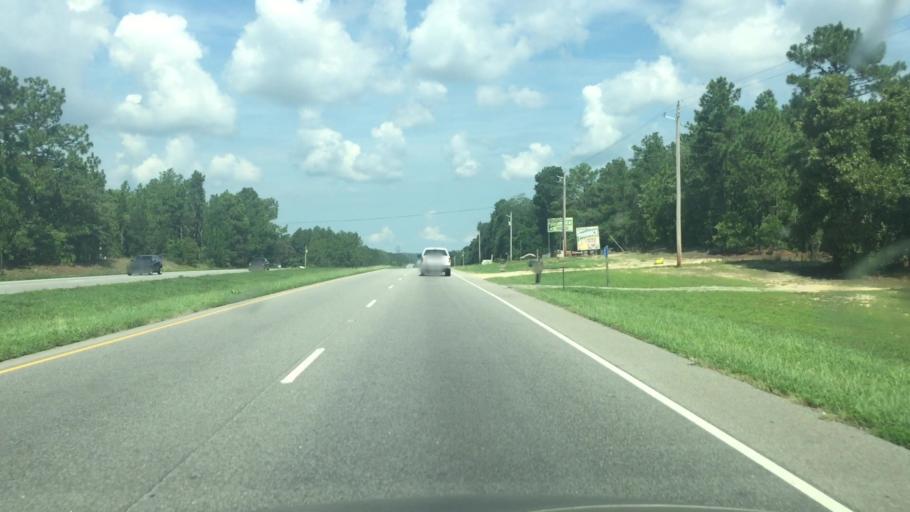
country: US
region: North Carolina
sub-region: Scotland County
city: Laurel Hill
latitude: 34.8410
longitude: -79.6034
